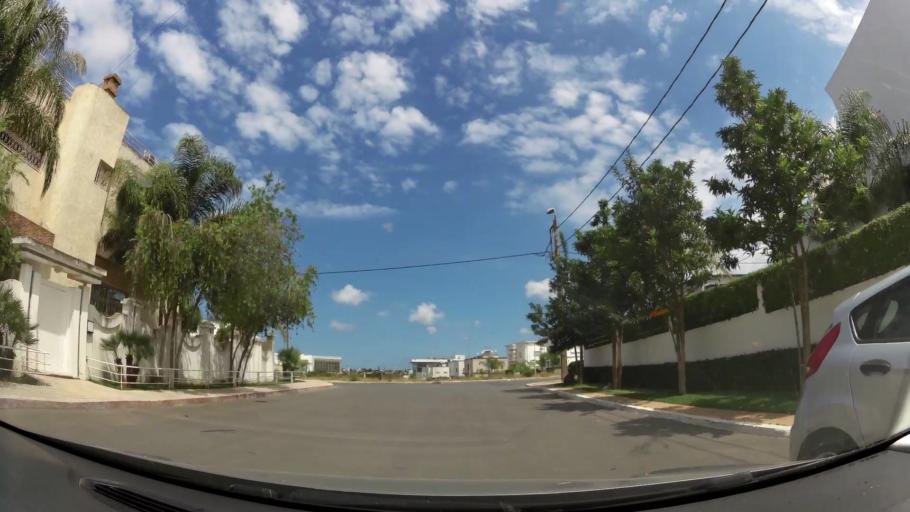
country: MA
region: Gharb-Chrarda-Beni Hssen
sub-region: Kenitra Province
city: Kenitra
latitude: 34.2517
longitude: -6.5980
